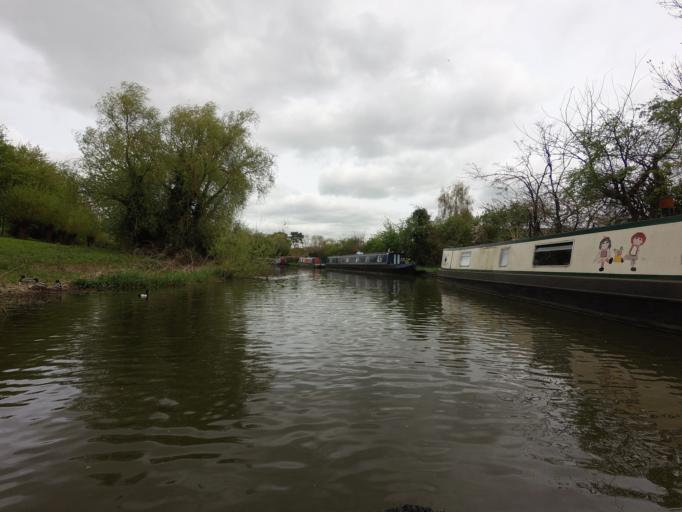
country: GB
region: England
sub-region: Milton Keynes
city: Simpson
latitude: 52.0170
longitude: -0.7180
